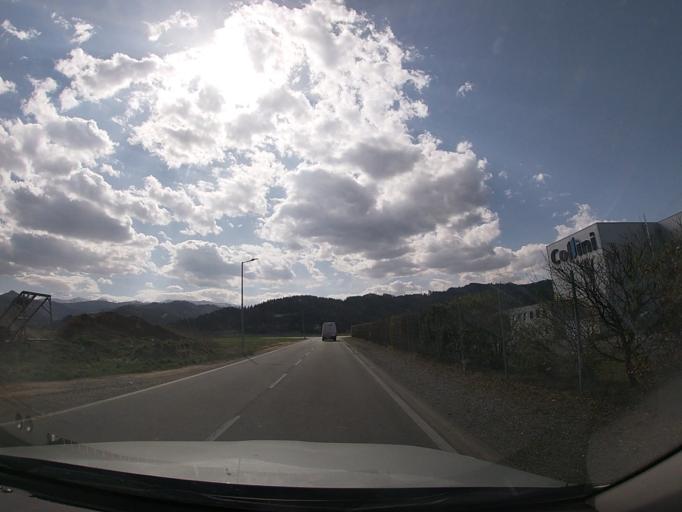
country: AT
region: Styria
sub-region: Politischer Bezirk Murtal
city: Judenburg
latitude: 47.1853
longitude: 14.6661
